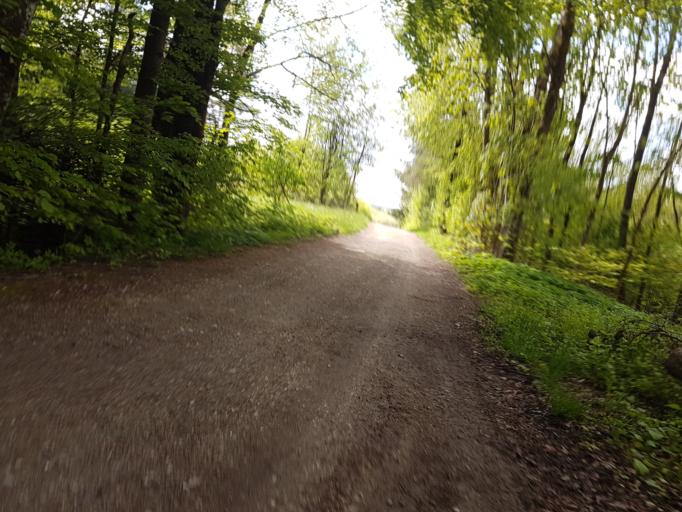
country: CH
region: Solothurn
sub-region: Bezirk Olten
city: Gunzgen
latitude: 47.3042
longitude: 7.8451
